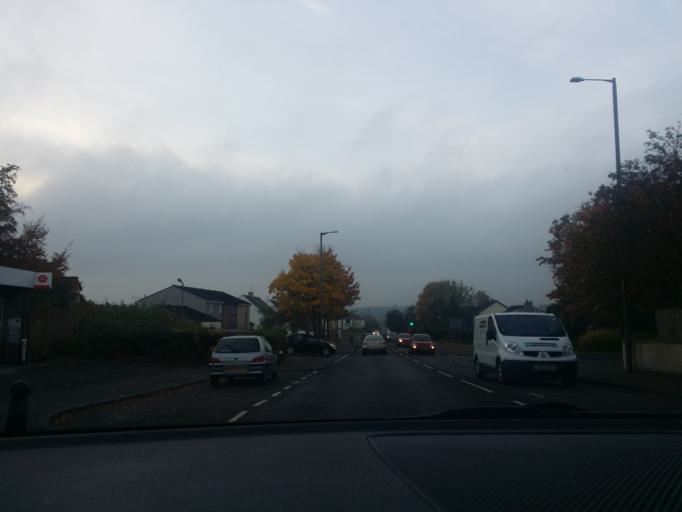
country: GB
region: Scotland
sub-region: Stirling
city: Bannockburn
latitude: 56.0924
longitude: -3.9329
